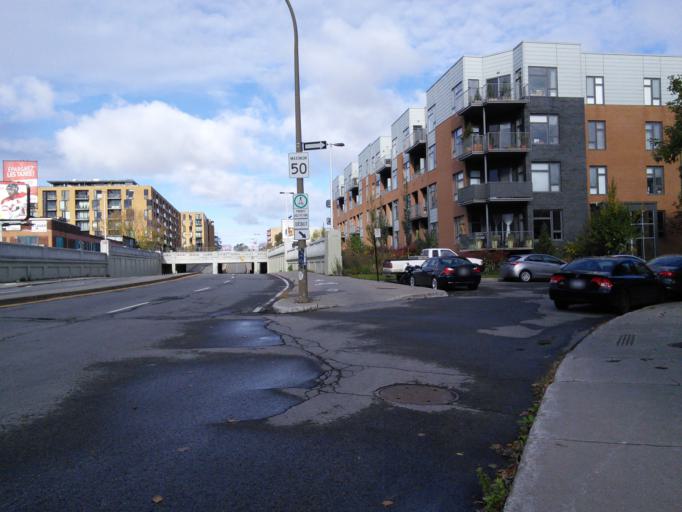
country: CA
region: Quebec
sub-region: Montreal
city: Montreal
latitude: 45.5312
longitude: -73.5925
